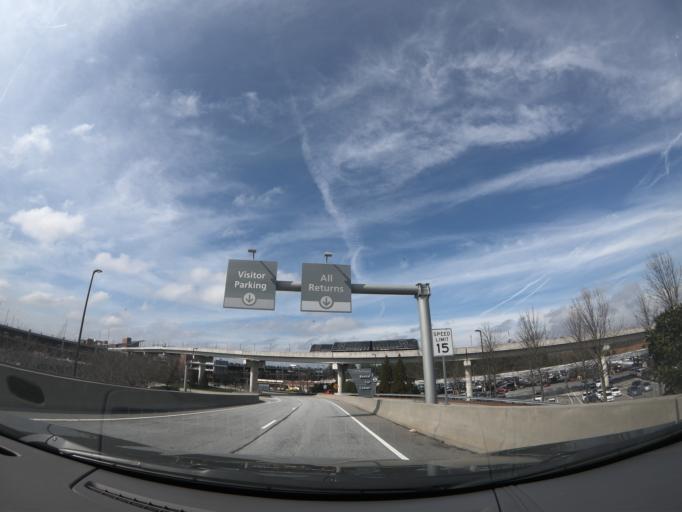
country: US
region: Georgia
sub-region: Fulton County
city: College Park
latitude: 33.6393
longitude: -84.4608
